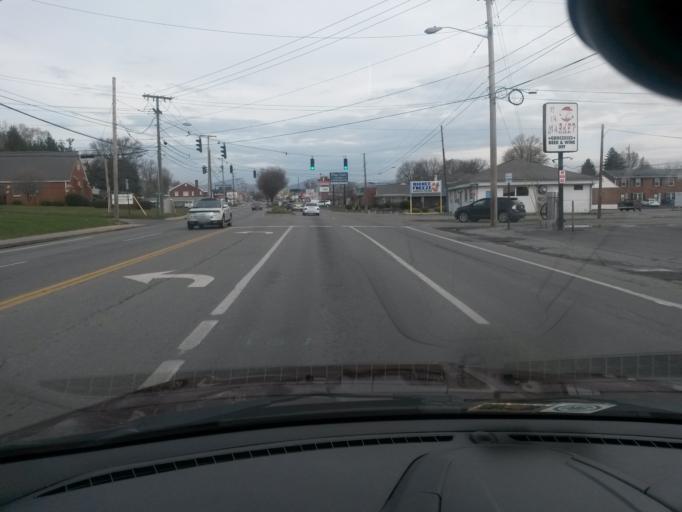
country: US
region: Virginia
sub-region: Roanoke County
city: Hollins
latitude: 37.3123
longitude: -79.9513
